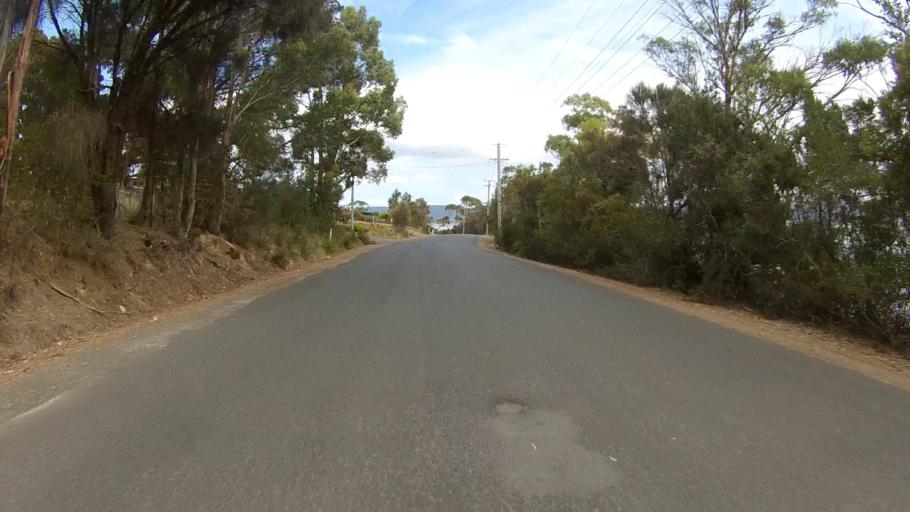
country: AU
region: Tasmania
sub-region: Kingborough
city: Margate
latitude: -43.0236
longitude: 147.2911
